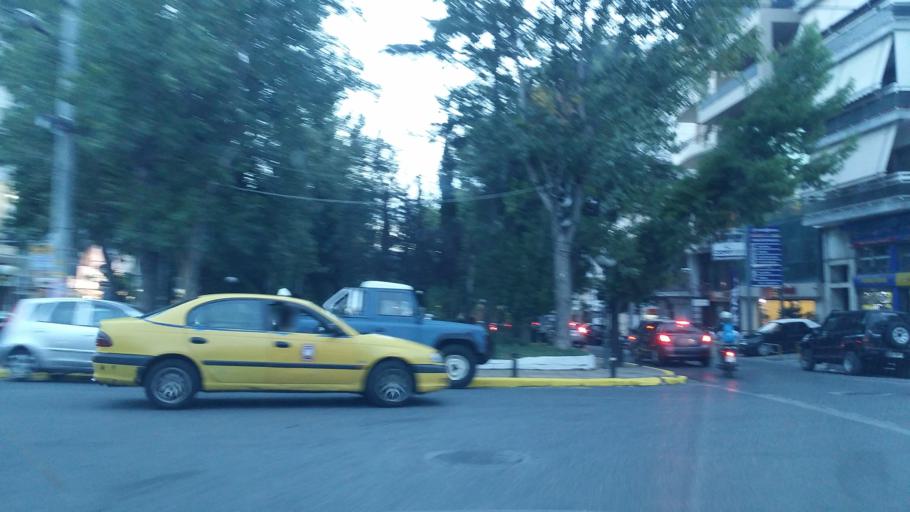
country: GR
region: Attica
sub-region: Nomarchia Athinas
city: Nea Ionia
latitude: 38.0453
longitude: 23.7514
